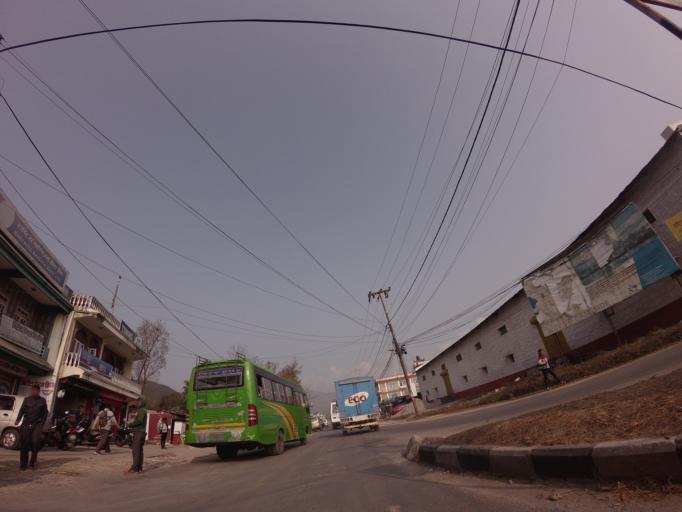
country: NP
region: Western Region
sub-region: Gandaki Zone
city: Pokhara
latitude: 28.1924
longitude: 83.9713
